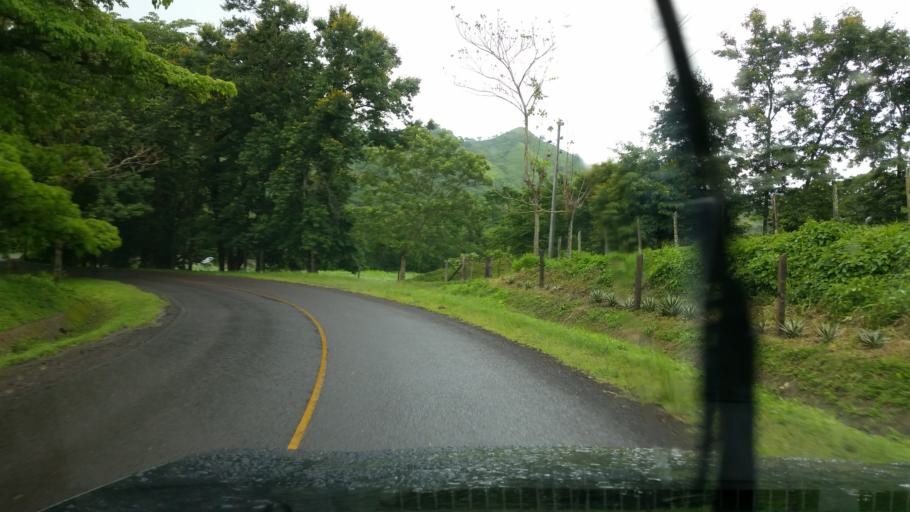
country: NI
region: Matagalpa
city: San Ramon
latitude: 13.0432
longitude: -85.7679
